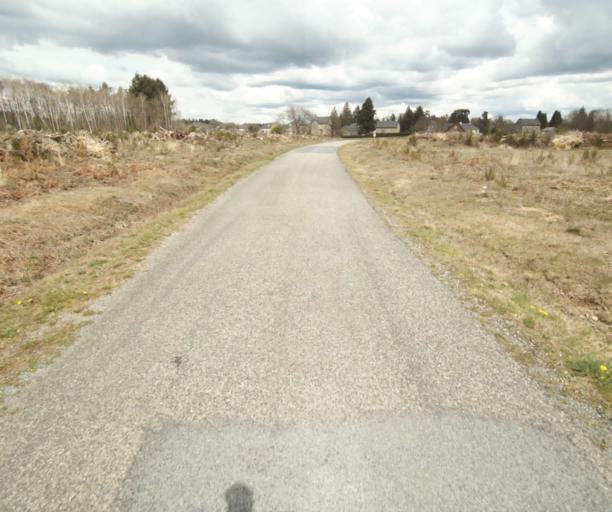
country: FR
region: Limousin
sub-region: Departement de la Correze
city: Correze
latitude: 45.3378
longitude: 1.9293
